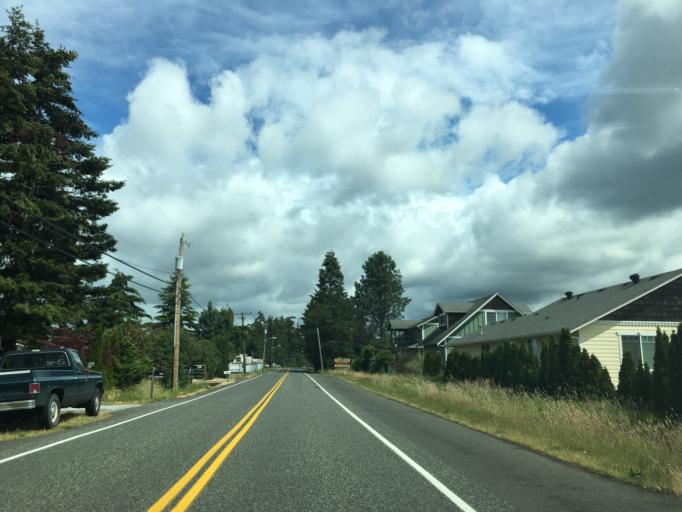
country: US
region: Washington
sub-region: Whatcom County
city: Birch Bay
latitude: 48.9089
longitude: -122.7486
